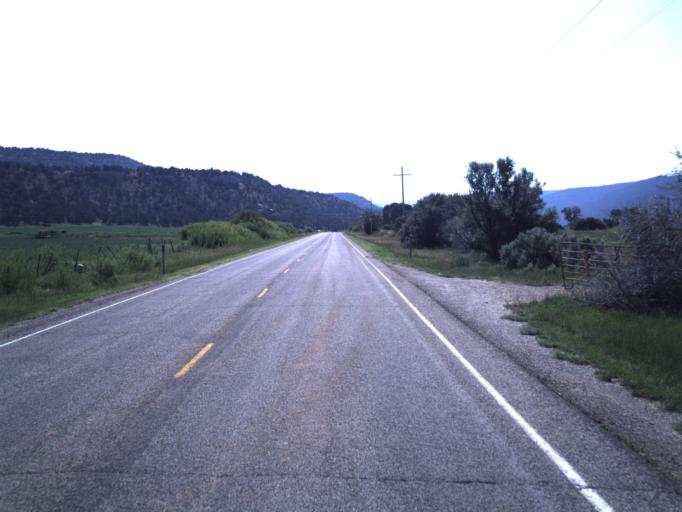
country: US
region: Utah
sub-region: Duchesne County
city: Duchesne
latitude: 40.3358
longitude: -110.6805
